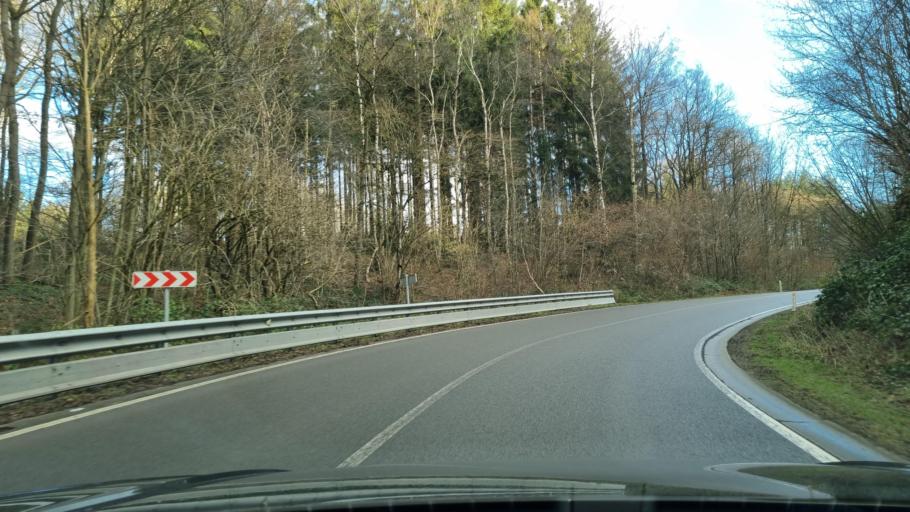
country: BE
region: Wallonia
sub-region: Province de Liege
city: Limbourg
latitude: 50.5753
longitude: 5.9153
